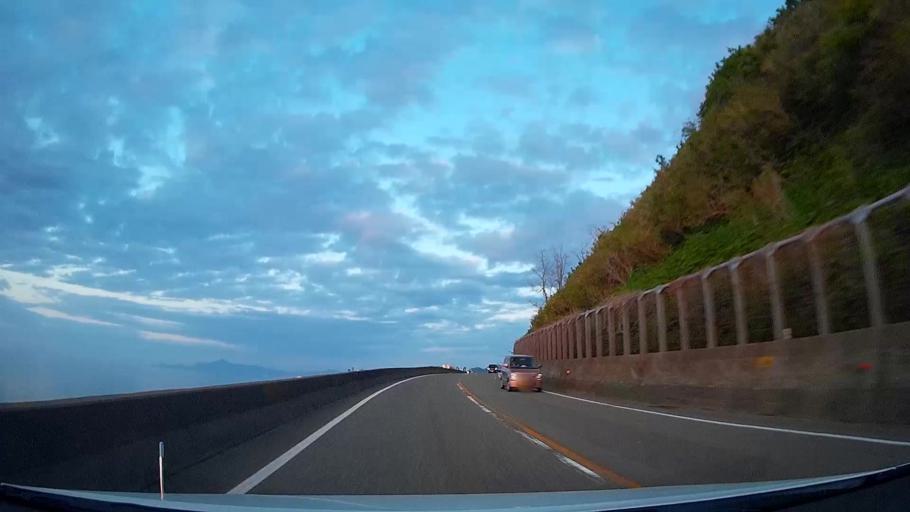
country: JP
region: Niigata
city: Joetsu
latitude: 37.1705
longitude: 138.1190
